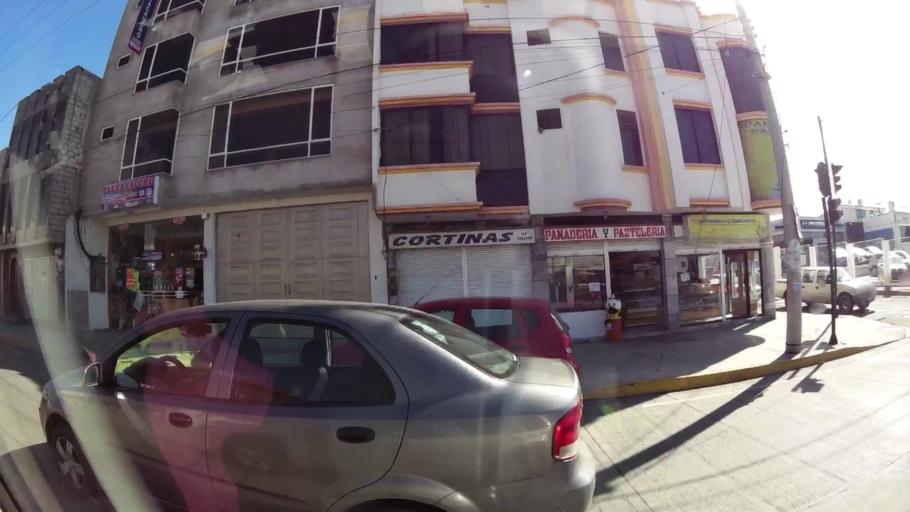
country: EC
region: Chimborazo
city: Riobamba
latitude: -1.6556
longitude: -78.6650
